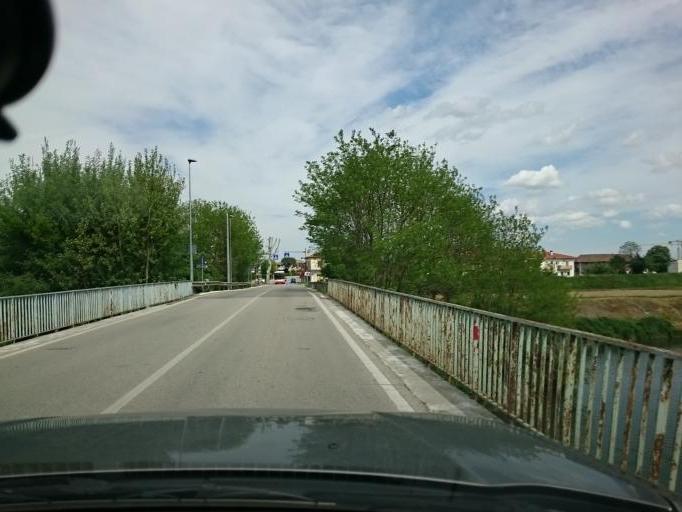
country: IT
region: Veneto
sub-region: Provincia di Vicenza
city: Longare
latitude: 45.4807
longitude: 11.6120
